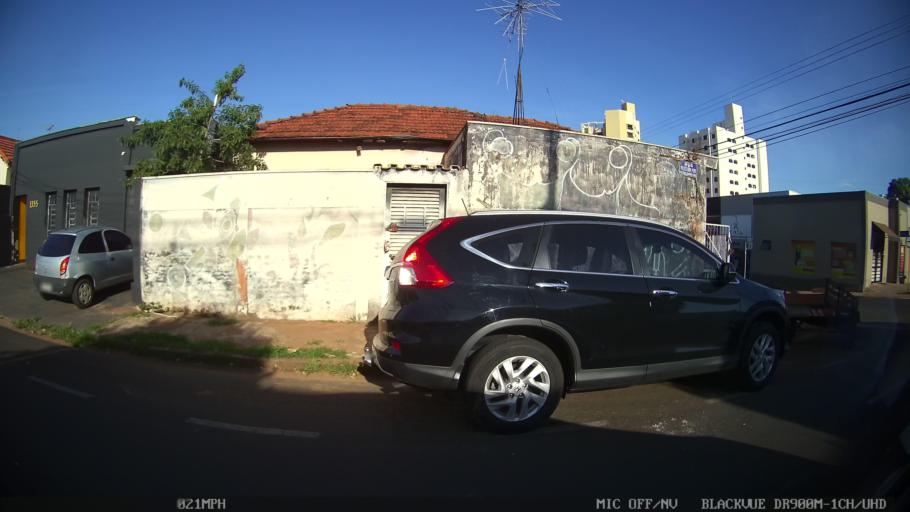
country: BR
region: Sao Paulo
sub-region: Sao Jose Do Rio Preto
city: Sao Jose do Rio Preto
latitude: -20.8102
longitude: -49.3889
